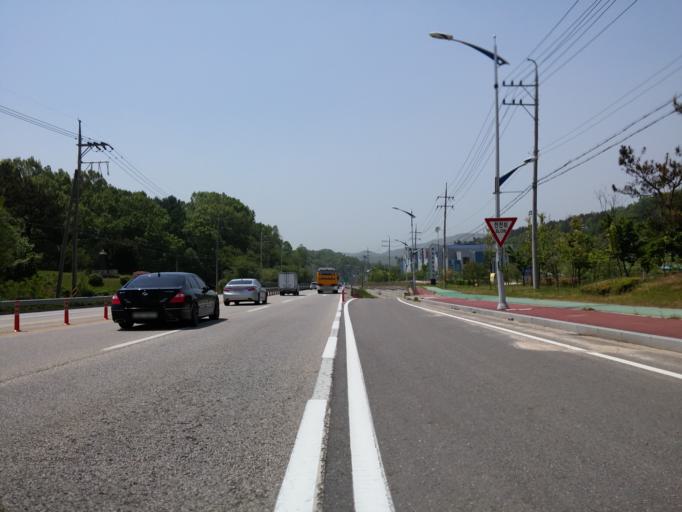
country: KR
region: Chungcheongnam-do
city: Nonsan
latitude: 36.2727
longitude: 127.2352
